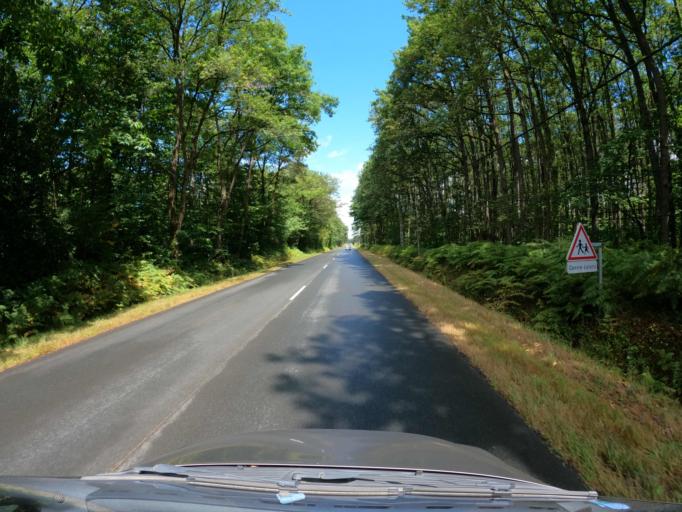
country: FR
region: Pays de la Loire
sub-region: Departement de Maine-et-Loire
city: Feneu
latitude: 47.5800
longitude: -0.5919
